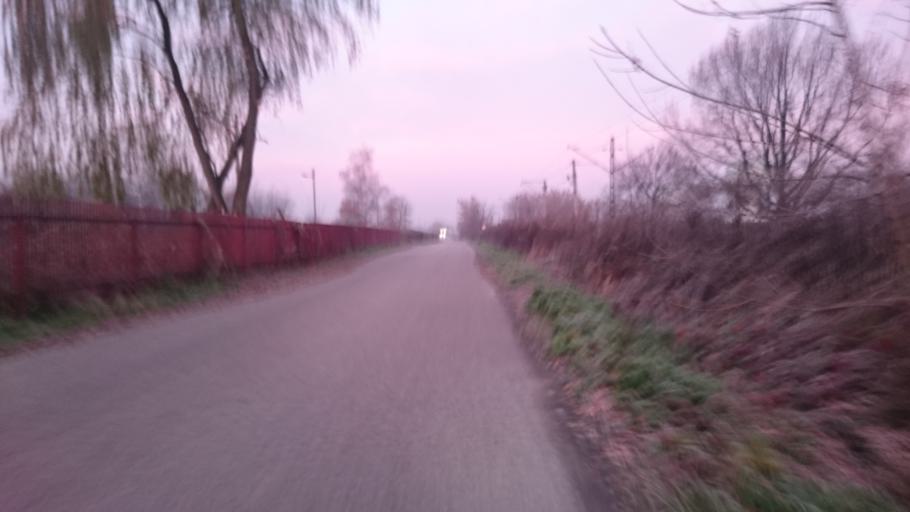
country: PL
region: Lesser Poland Voivodeship
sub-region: Powiat wielicki
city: Czarnochowice
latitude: 50.0253
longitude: 20.0191
